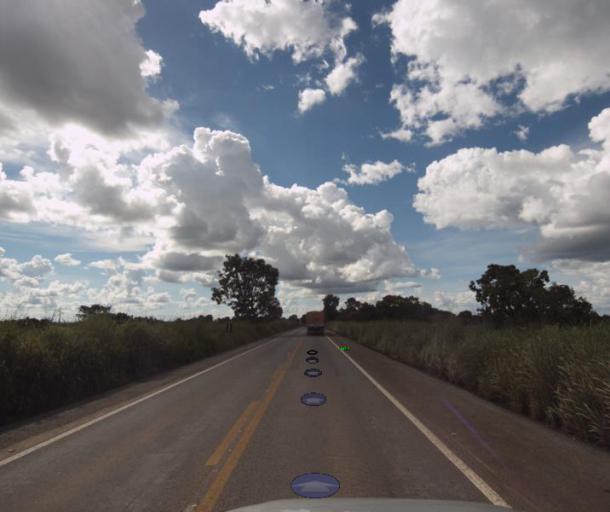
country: BR
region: Goias
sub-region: Porangatu
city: Porangatu
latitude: -13.2347
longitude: -49.1440
